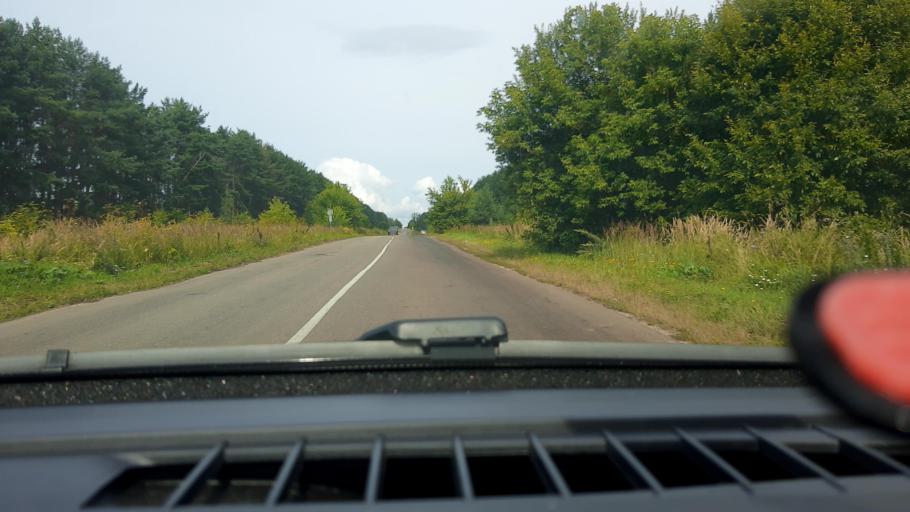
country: RU
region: Nizjnij Novgorod
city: Bogorodsk
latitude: 56.0835
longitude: 43.5700
